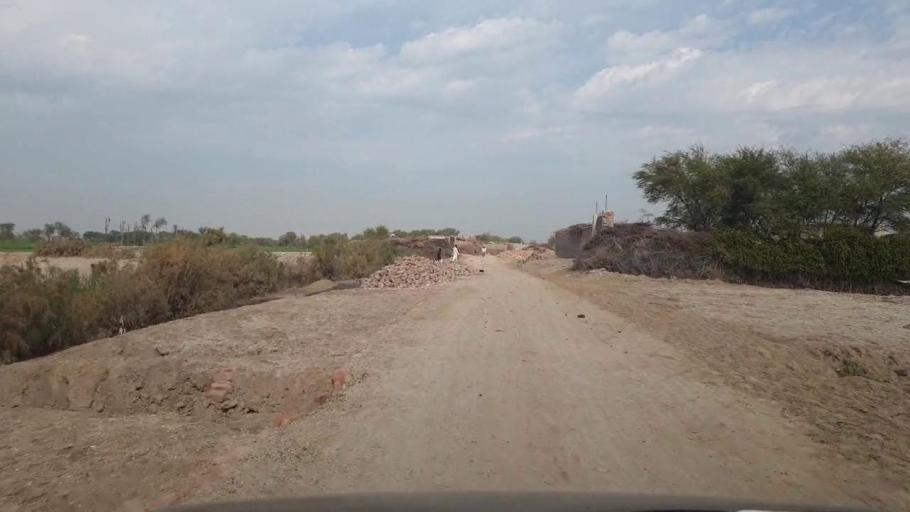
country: PK
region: Sindh
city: Sakrand
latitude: 26.0028
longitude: 68.4003
